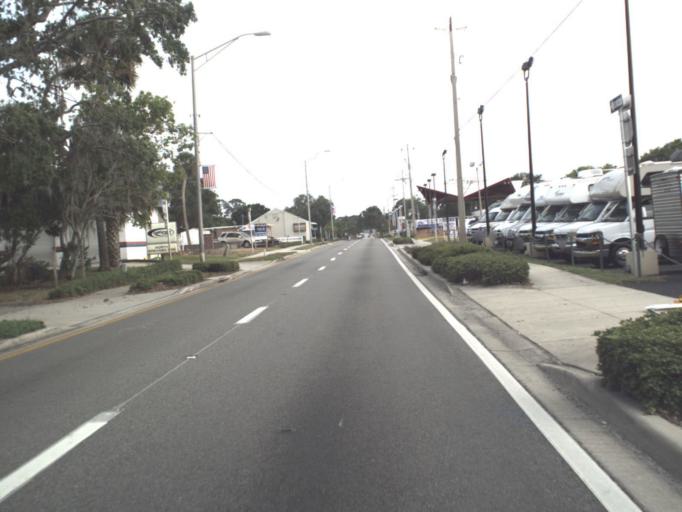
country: US
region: Florida
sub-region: Brevard County
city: Titusville
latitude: 28.6056
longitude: -80.8085
